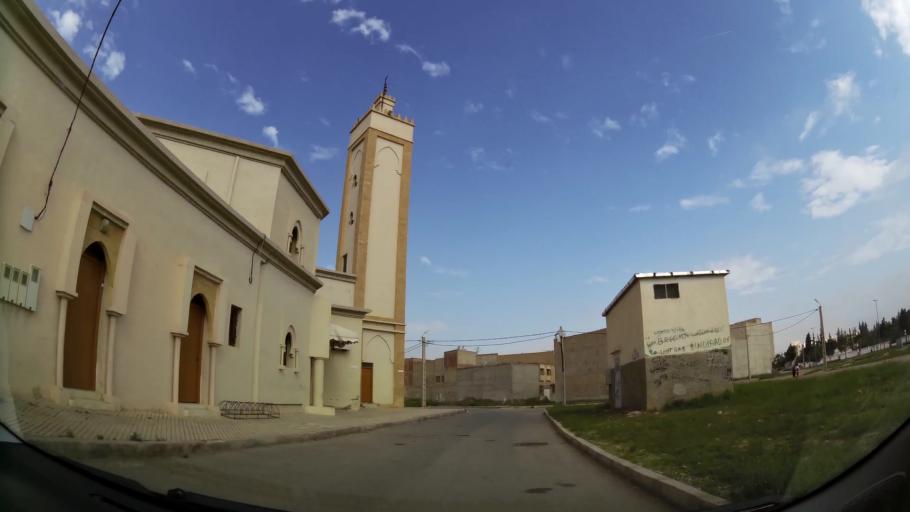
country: MA
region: Oriental
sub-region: Oujda-Angad
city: Oujda
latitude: 34.6923
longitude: -1.9002
